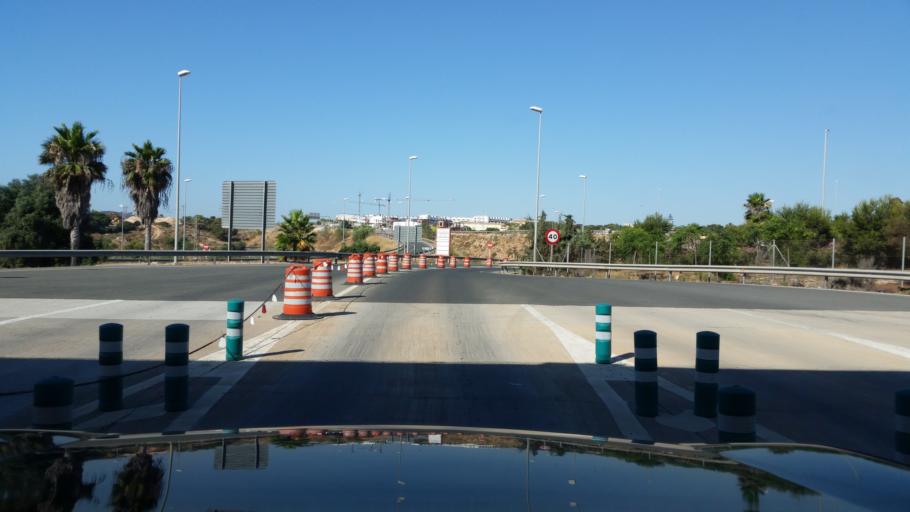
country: ES
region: Valencia
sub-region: Provincia de Alicante
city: San Miguel de Salinas
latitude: 37.9259
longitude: -0.7375
